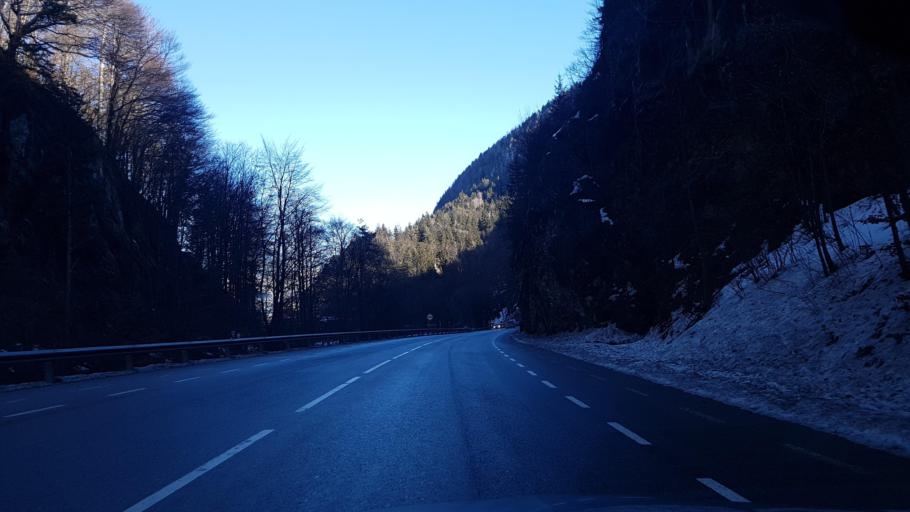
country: AT
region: Tyrol
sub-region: Politischer Bezirk Kufstein
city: Kufstein
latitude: 47.5630
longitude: 12.1559
